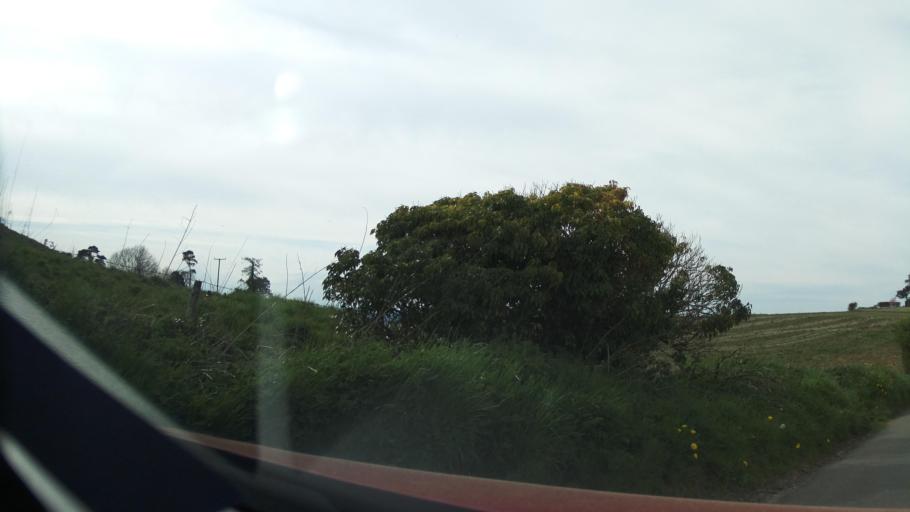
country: GB
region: England
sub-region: Dorset
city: Sherborne
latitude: 50.9891
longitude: -2.5167
